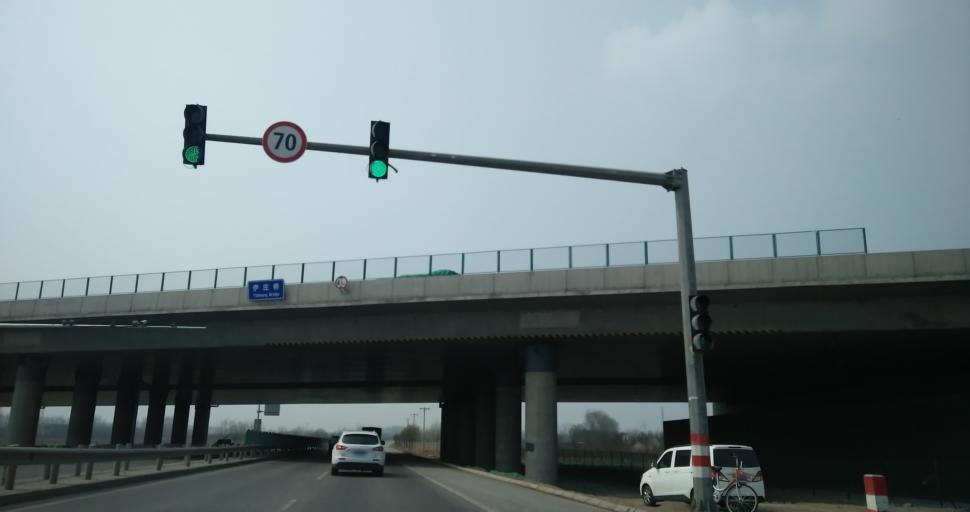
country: CN
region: Beijing
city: Qingyundian
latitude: 39.6837
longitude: 116.4505
